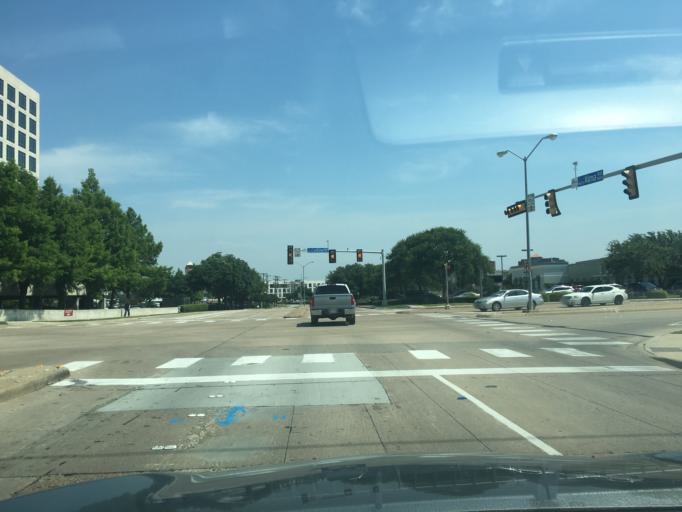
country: US
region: Texas
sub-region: Dallas County
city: Richardson
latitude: 32.9676
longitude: -96.7171
